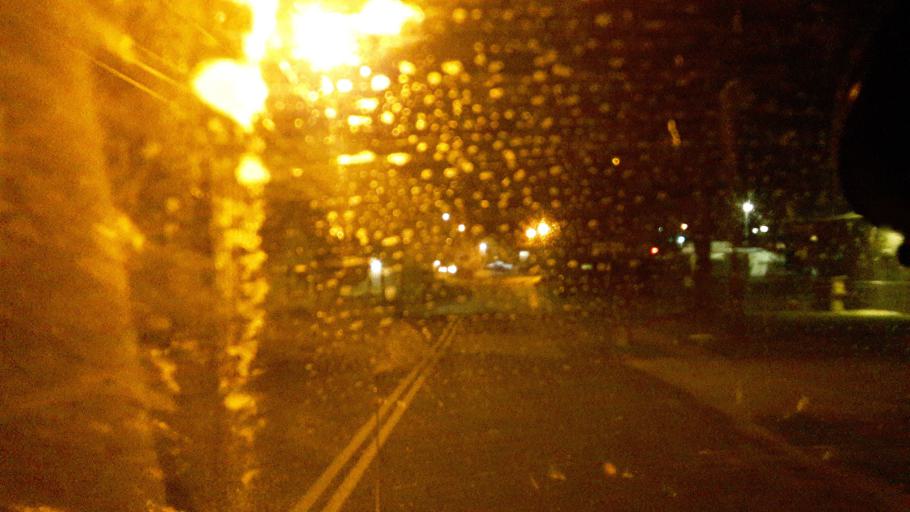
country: US
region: North Carolina
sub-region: Forsyth County
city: Winston-Salem
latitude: 36.0711
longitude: -80.2314
